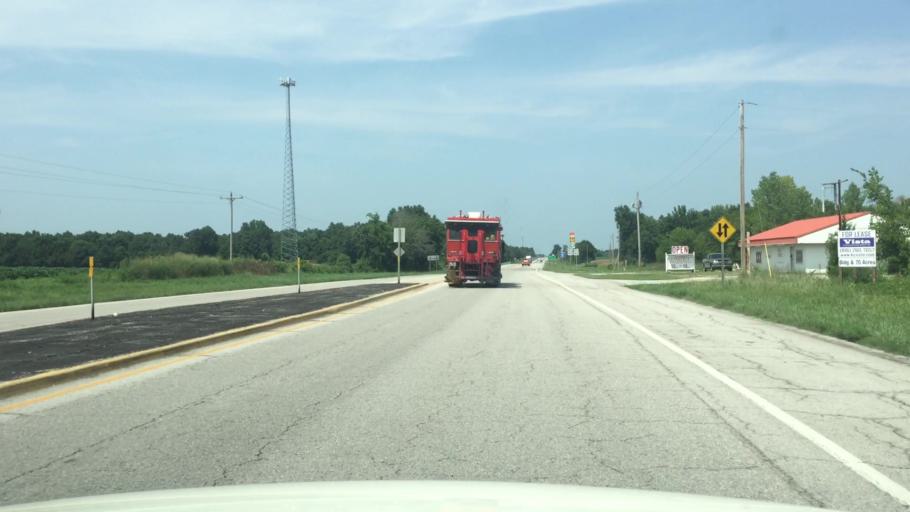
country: US
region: Kansas
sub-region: Cherokee County
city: Galena
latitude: 37.1793
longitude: -94.7044
